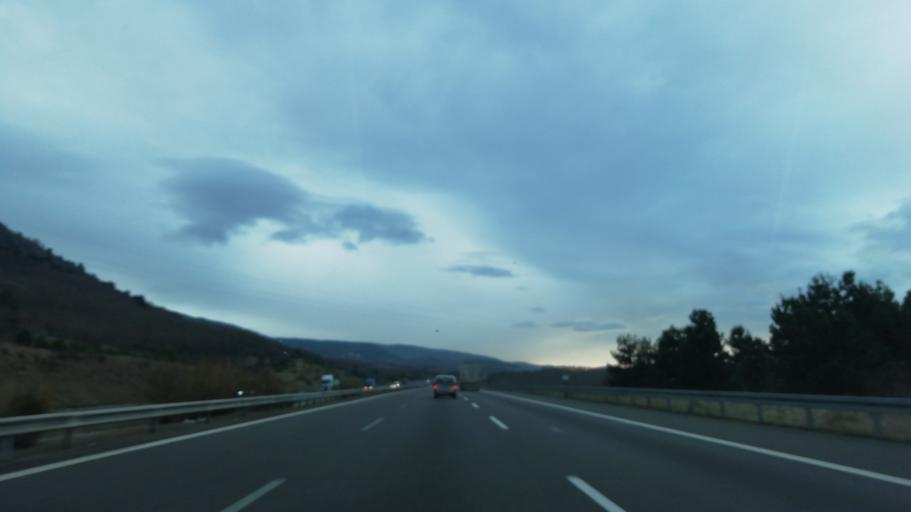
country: TR
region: Bolu
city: Yenicaga
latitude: 40.7572
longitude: 31.9687
